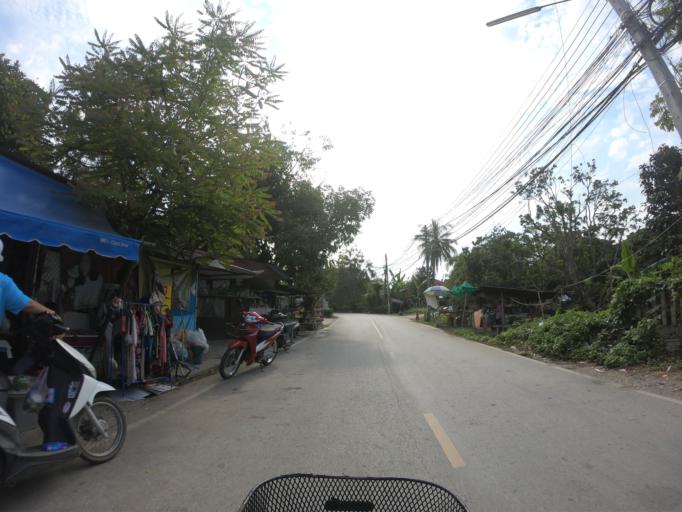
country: TH
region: Chiang Mai
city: Saraphi
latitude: 18.7281
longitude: 99.0632
